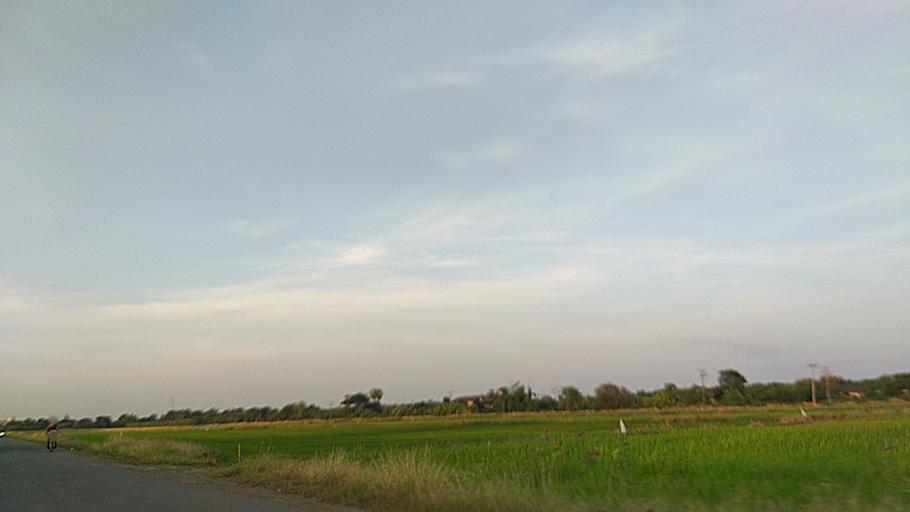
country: TH
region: Pathum Thani
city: Nong Suea
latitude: 14.0585
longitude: 100.8676
